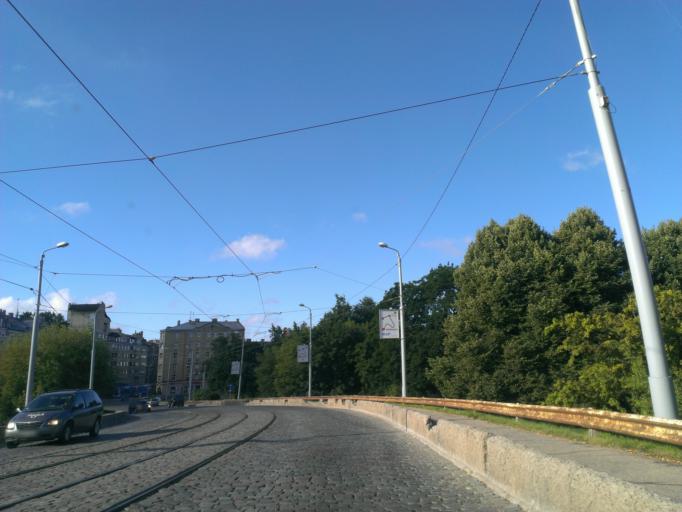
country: LV
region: Riga
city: Riga
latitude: 56.9778
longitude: 24.1453
